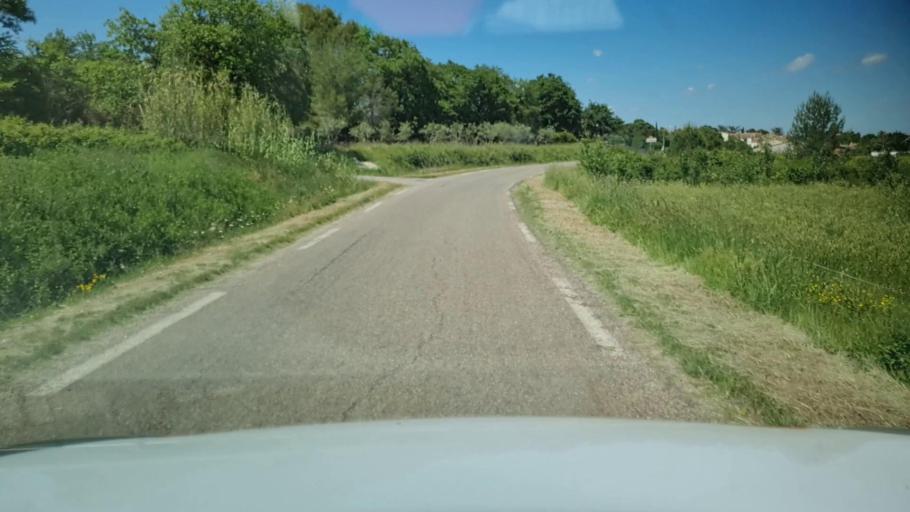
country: FR
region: Languedoc-Roussillon
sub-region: Departement du Gard
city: Saint-Mamert-du-Gard
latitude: 43.9024
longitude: 4.1919
